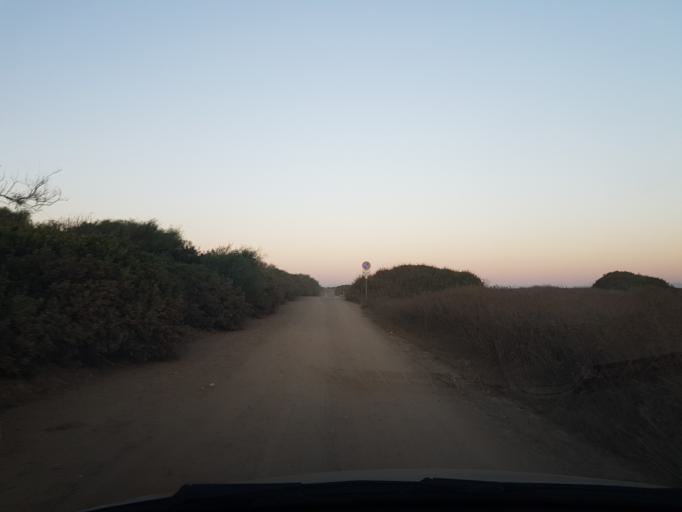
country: IT
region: Sardinia
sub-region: Provincia di Oristano
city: Riola Sardo
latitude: 40.0412
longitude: 8.3980
